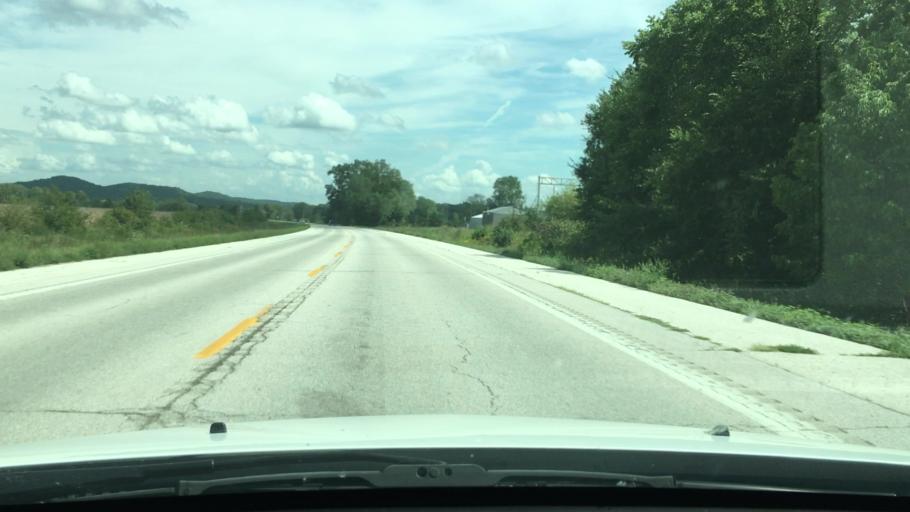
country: US
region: Missouri
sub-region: Pike County
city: Bowling Green
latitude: 39.3844
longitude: -91.1267
